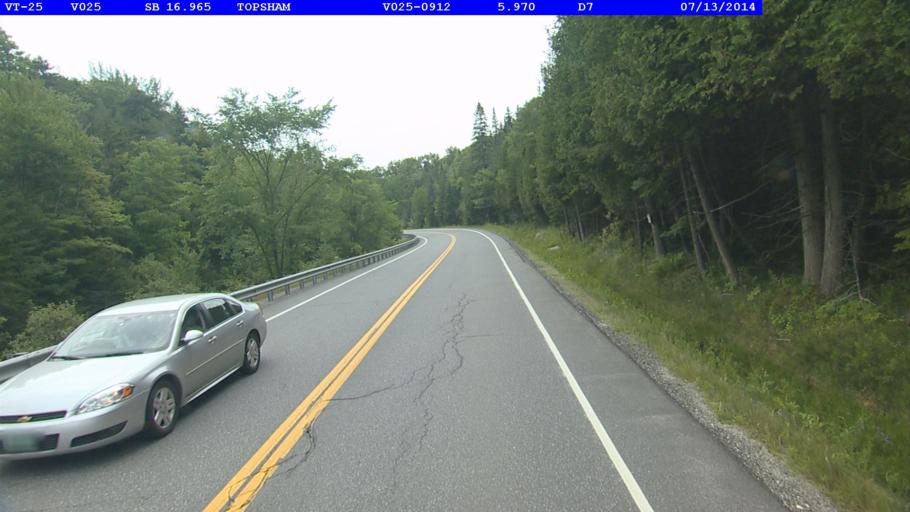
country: US
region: Vermont
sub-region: Orange County
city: Chelsea
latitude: 44.1310
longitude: -72.3132
